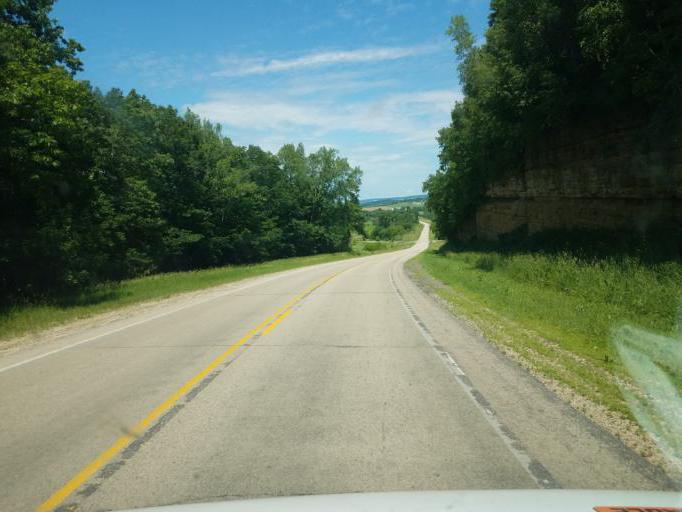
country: US
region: Wisconsin
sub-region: Vernon County
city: Hillsboro
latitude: 43.6006
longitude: -90.2649
